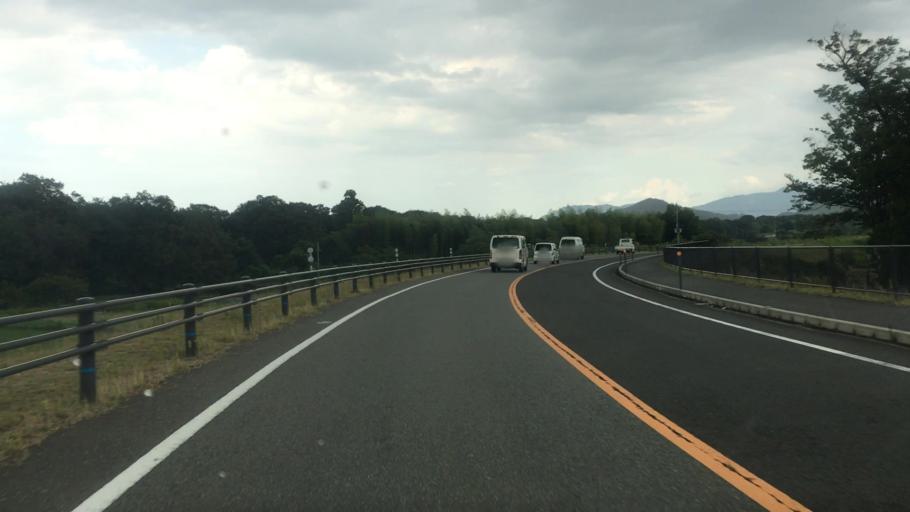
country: JP
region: Hyogo
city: Toyooka
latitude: 35.4784
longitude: 134.7923
